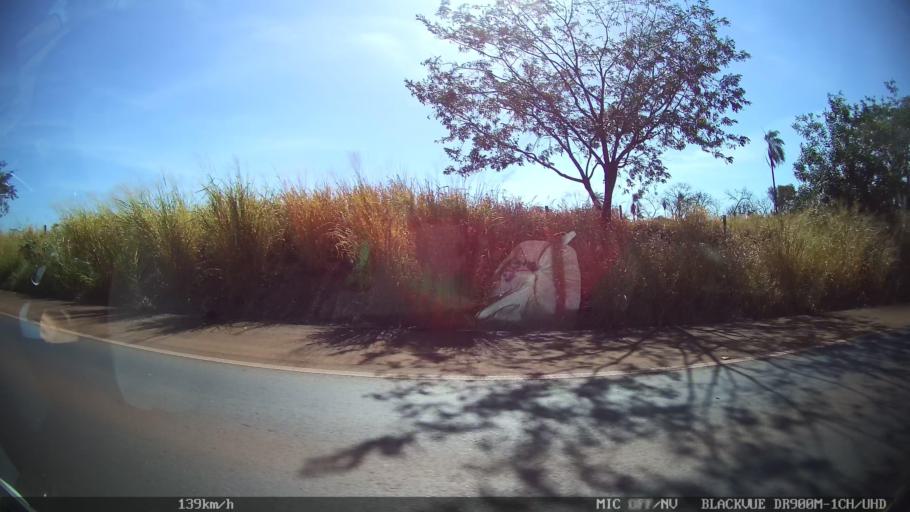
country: BR
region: Sao Paulo
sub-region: Barretos
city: Barretos
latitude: -20.5235
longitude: -48.5834
